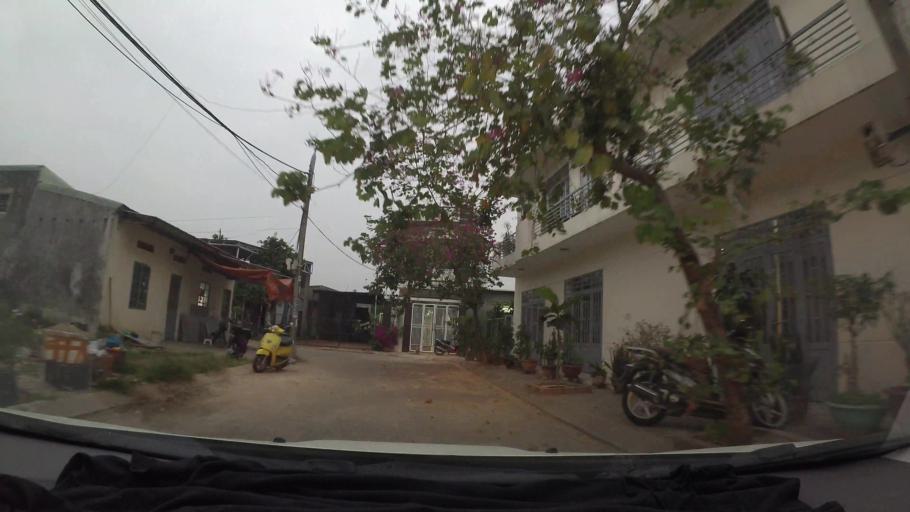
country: VN
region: Da Nang
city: Lien Chieu
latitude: 16.0551
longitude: 108.1706
